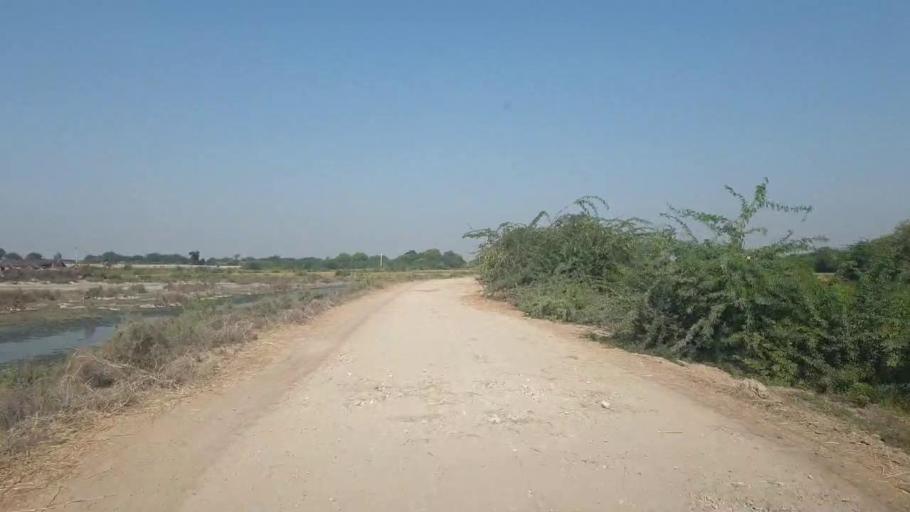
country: PK
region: Sindh
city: Badin
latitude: 24.6753
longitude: 68.8574
